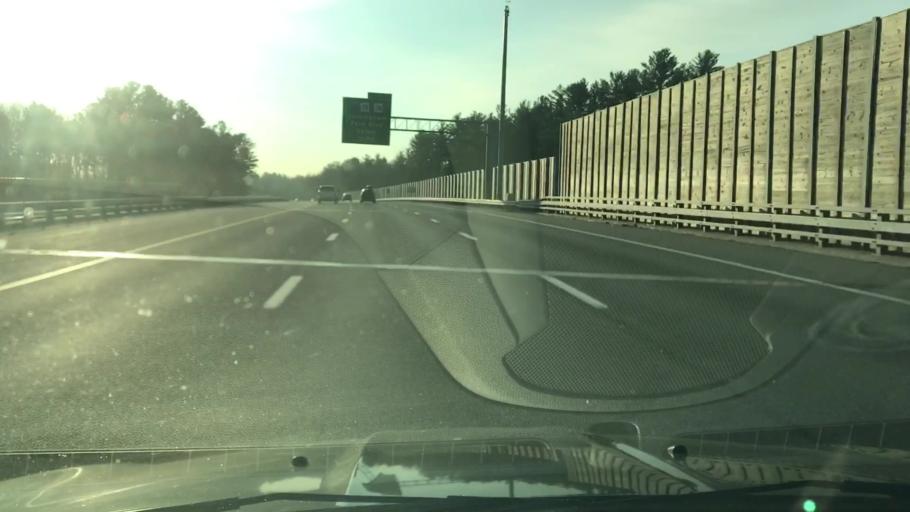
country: US
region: New Hampshire
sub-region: Rockingham County
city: Salem
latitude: 42.7651
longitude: -71.2386
